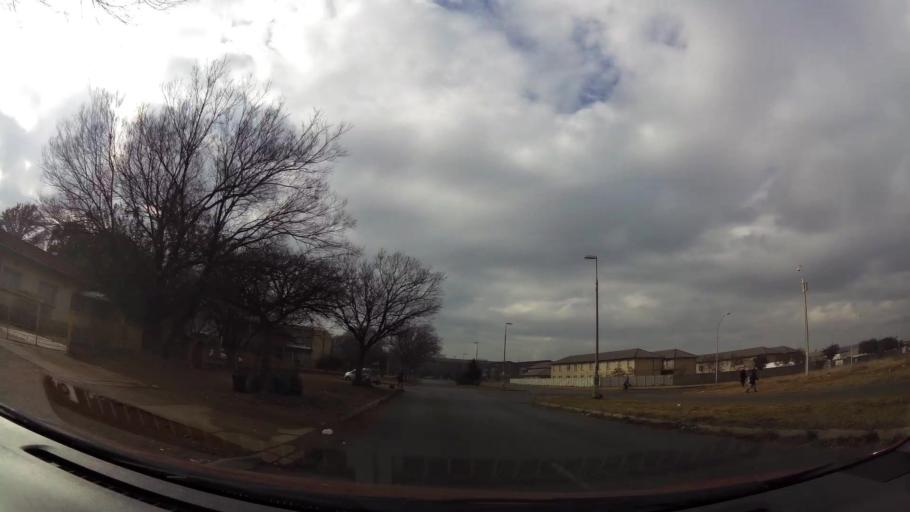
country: ZA
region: Gauteng
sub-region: Sedibeng District Municipality
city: Vanderbijlpark
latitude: -26.6932
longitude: 27.8383
